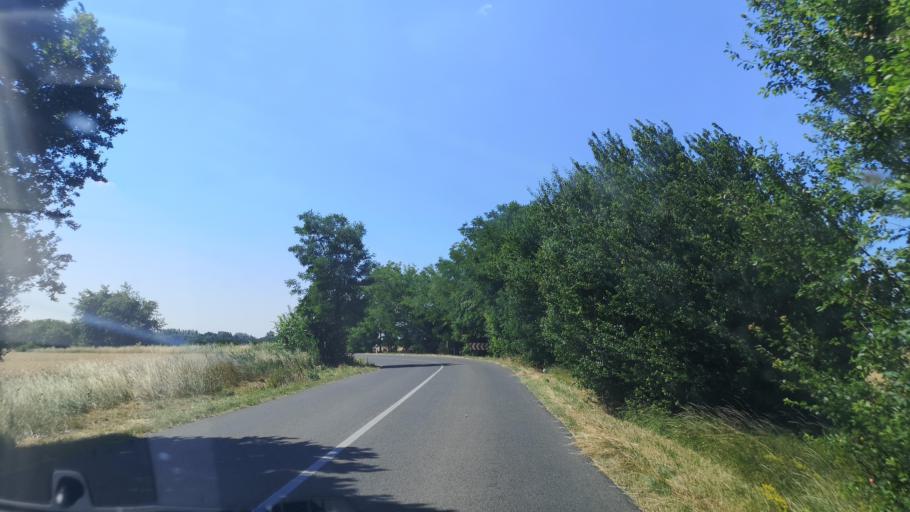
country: SK
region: Trnavsky
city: Dunajska Streda
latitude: 48.0759
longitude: 17.4884
